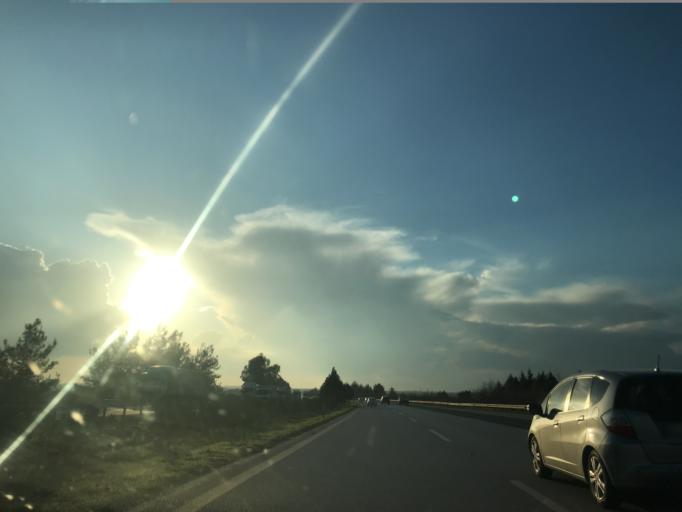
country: TR
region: Adana
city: Yakapinar
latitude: 37.0076
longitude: 35.6835
